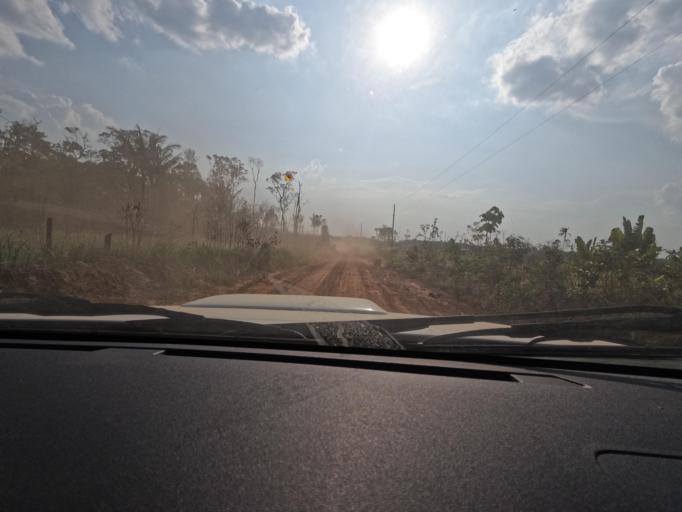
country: BR
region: Rondonia
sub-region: Porto Velho
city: Porto Velho
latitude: -8.5739
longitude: -64.0082
